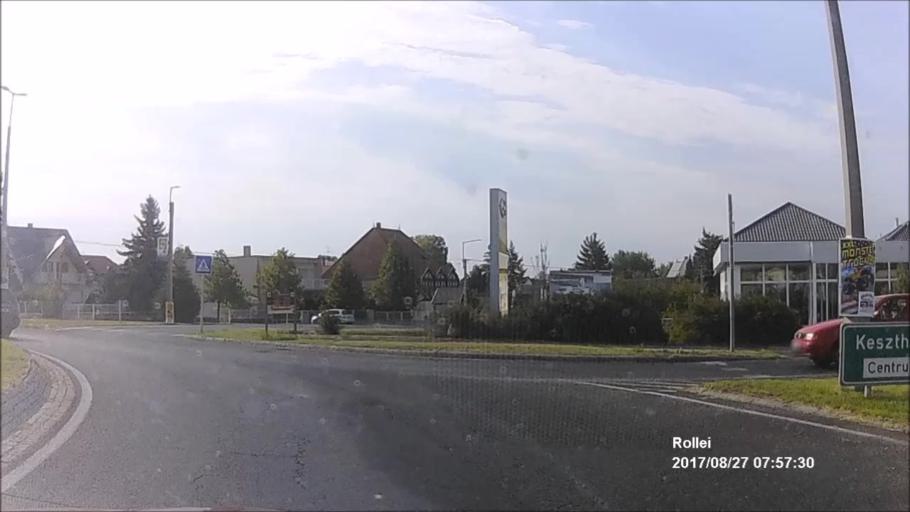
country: HU
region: Zala
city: Gyenesdias
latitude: 46.7738
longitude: 17.2773
